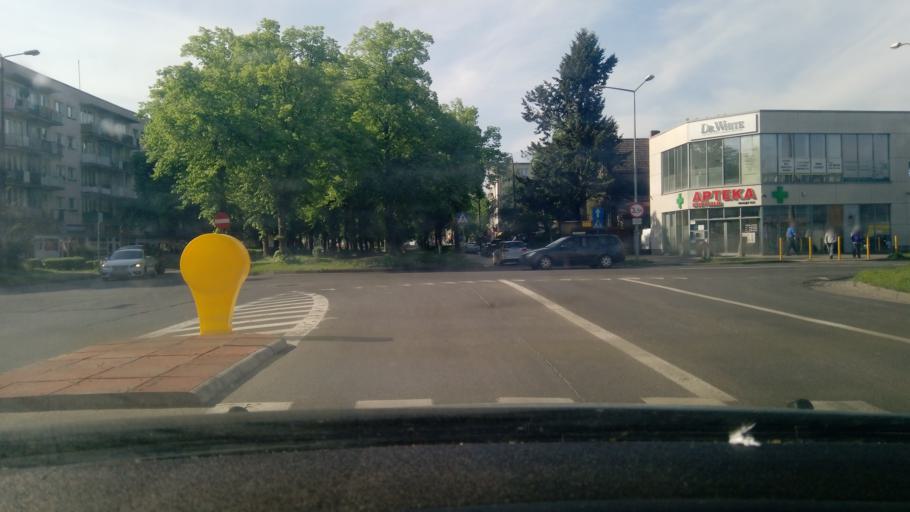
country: PL
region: Lubusz
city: Gorzow Wielkopolski
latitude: 52.7359
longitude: 15.2116
